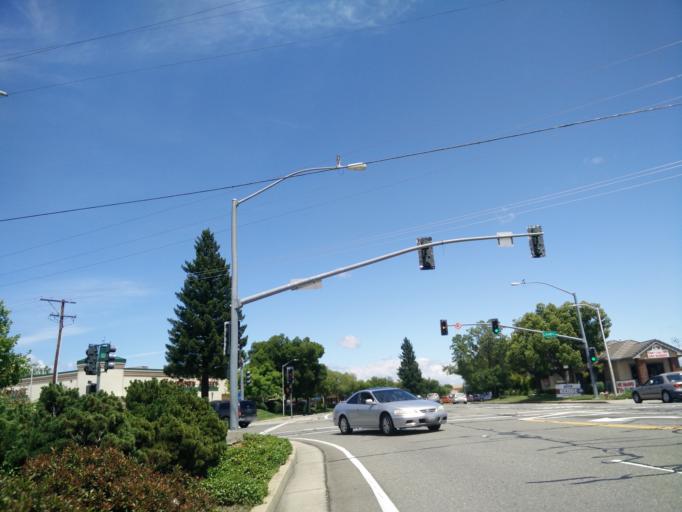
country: US
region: California
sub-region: Shasta County
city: Redding
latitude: 40.5860
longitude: -122.3536
